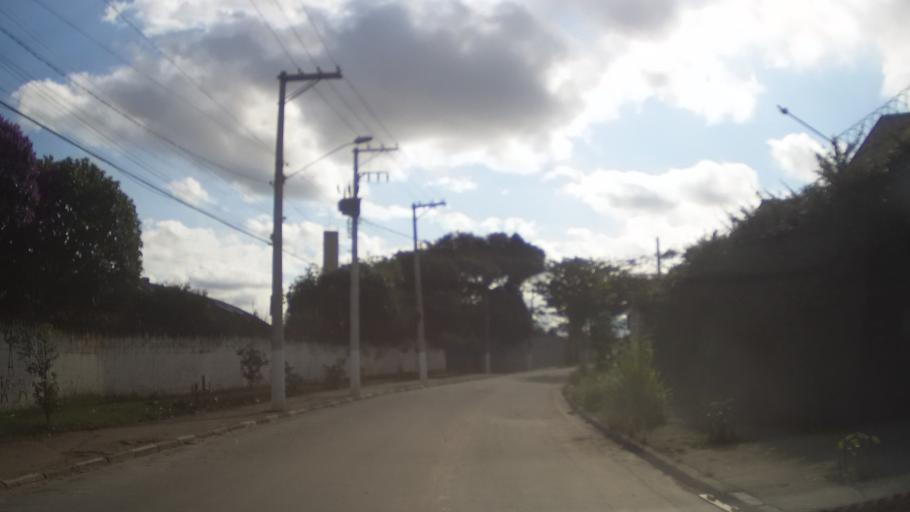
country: BR
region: Sao Paulo
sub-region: Guarulhos
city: Guarulhos
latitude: -23.4644
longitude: -46.4730
